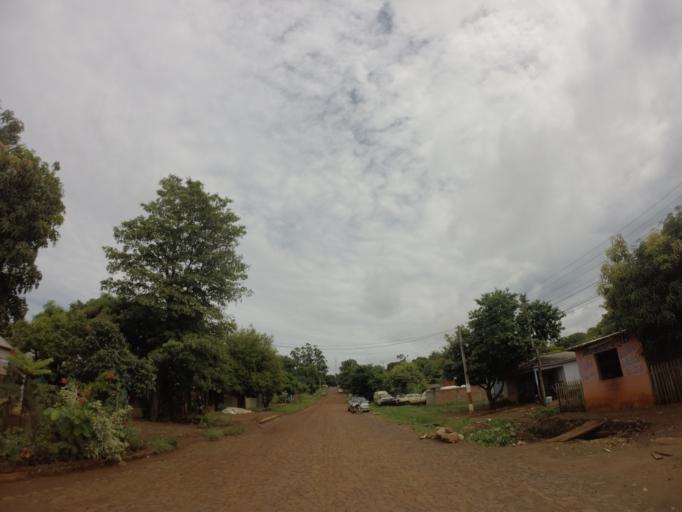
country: PY
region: Alto Parana
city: Ciudad del Este
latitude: -25.3940
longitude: -54.6442
